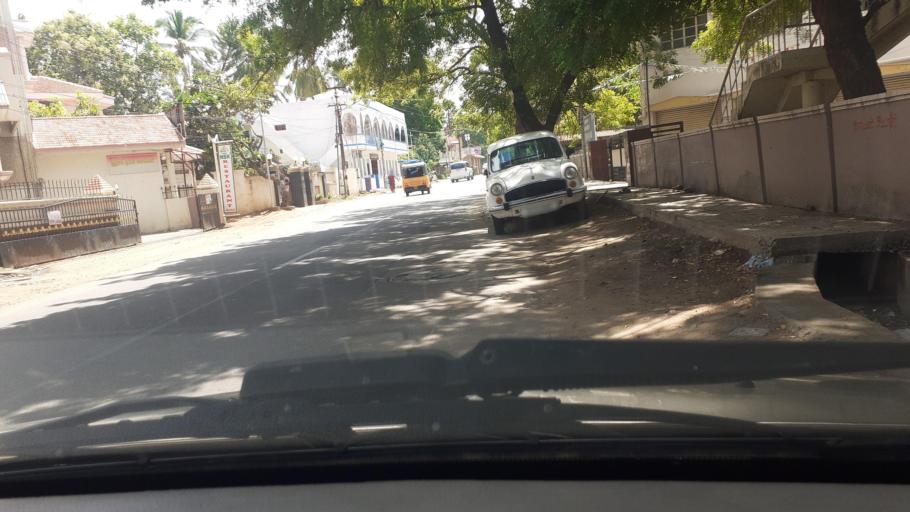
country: IN
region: Tamil Nadu
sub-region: Tirunelveli Kattabo
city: Tirunelveli
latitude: 8.7165
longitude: 77.7494
